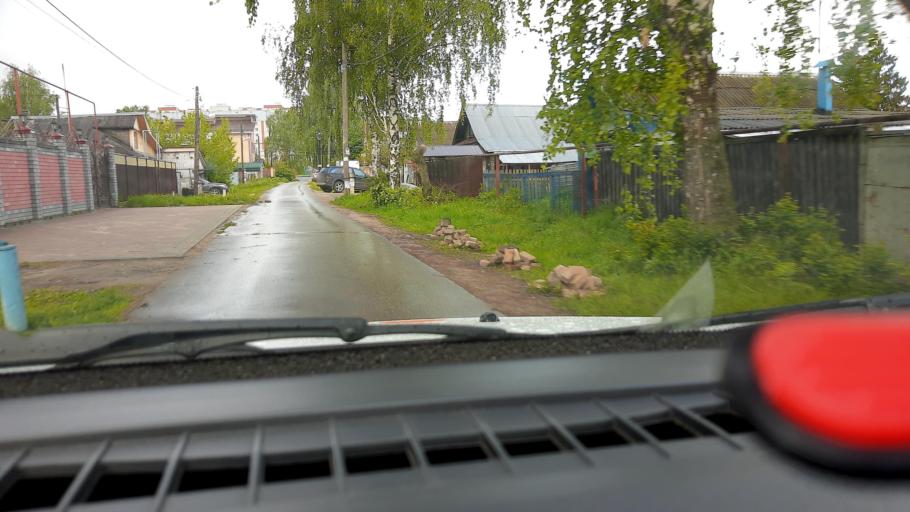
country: RU
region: Nizjnij Novgorod
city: Gorbatovka
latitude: 56.3622
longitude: 43.8407
